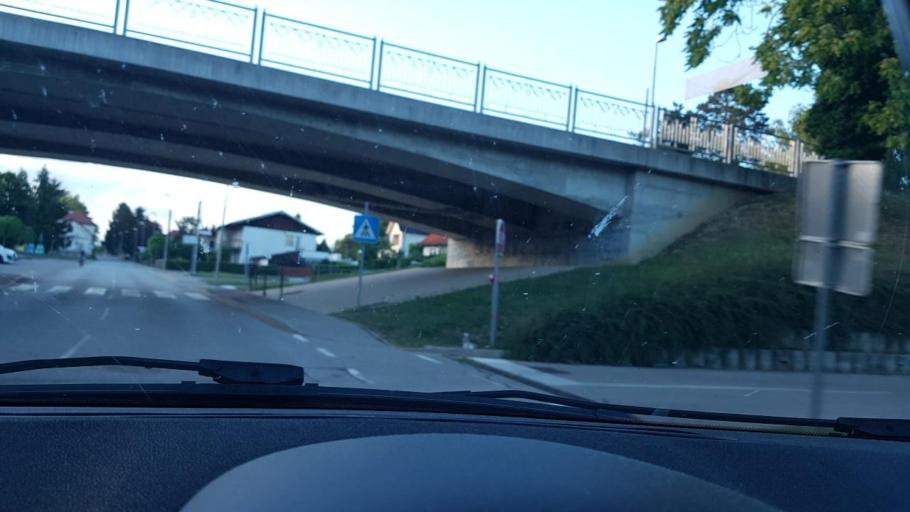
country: SI
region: Brezice
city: Brezice
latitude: 45.9038
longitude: 15.5942
